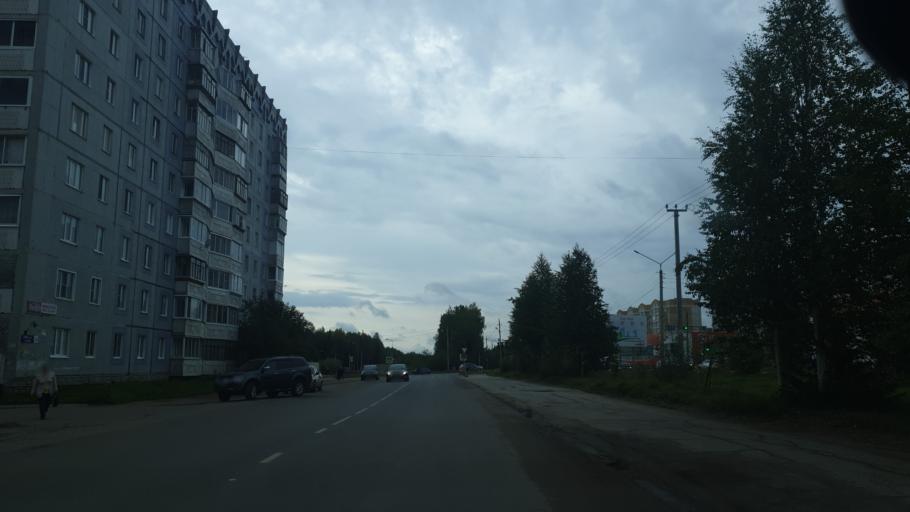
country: RU
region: Komi Republic
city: Ezhva
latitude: 61.7825
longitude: 50.7478
